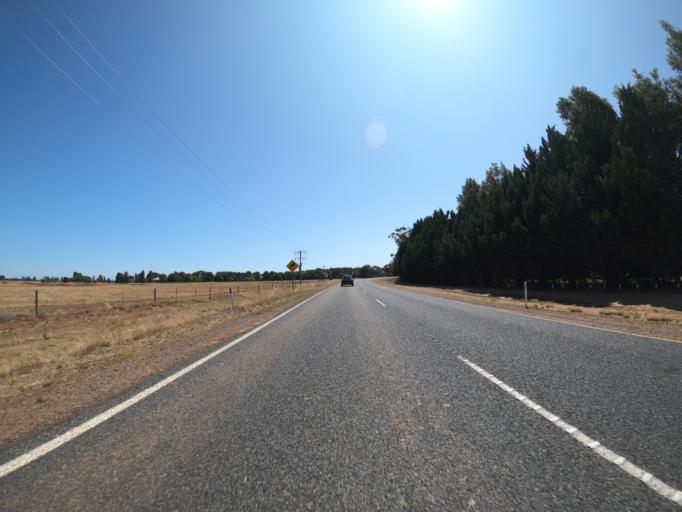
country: AU
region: Victoria
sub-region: Moira
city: Yarrawonga
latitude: -36.0277
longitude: 146.0755
